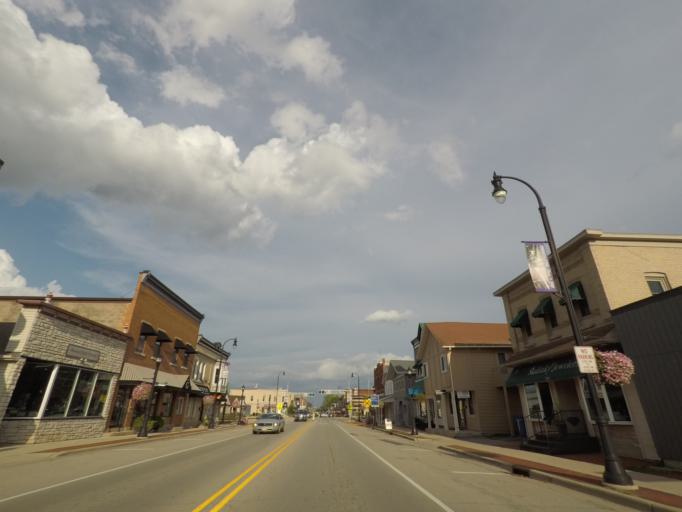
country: US
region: Wisconsin
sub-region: Dane County
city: Waunakee
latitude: 43.1919
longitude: -89.4561
